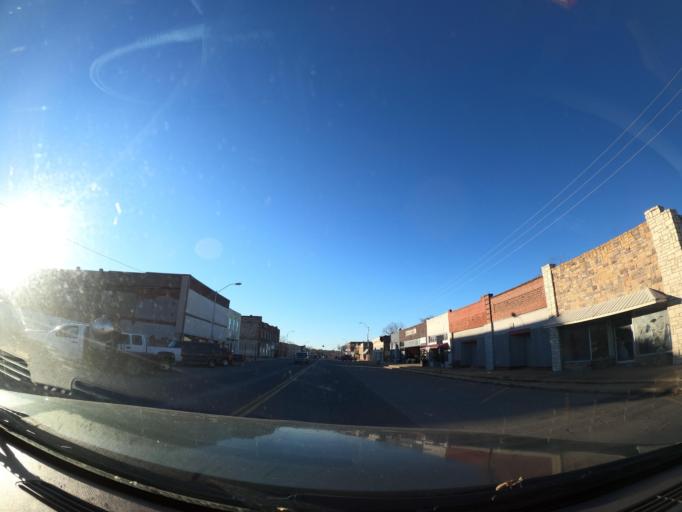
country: US
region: Oklahoma
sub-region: Pittsburg County
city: Hartshorne
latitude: 34.8452
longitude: -95.5565
